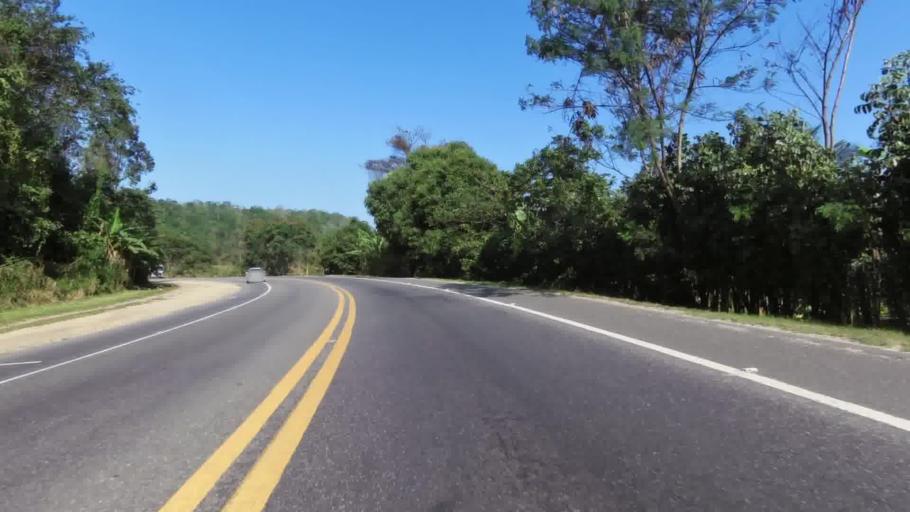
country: BR
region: Espirito Santo
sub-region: Rio Novo Do Sul
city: Rio Novo do Sul
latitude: -20.8664
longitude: -40.8960
